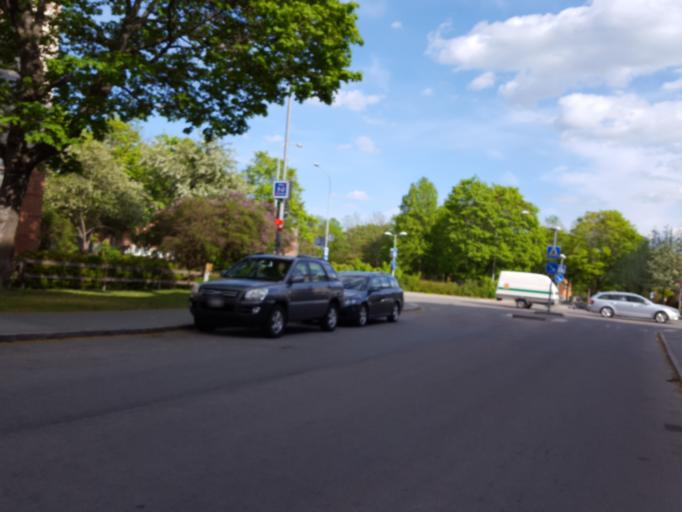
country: SE
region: Uppsala
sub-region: Uppsala Kommun
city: Uppsala
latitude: 59.8672
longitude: 17.6657
